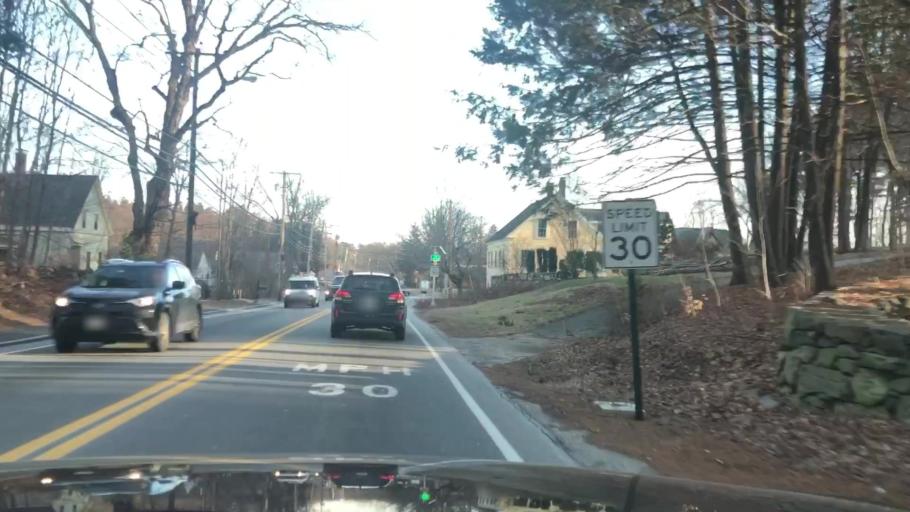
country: US
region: Massachusetts
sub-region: Worcester County
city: Bolton
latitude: 42.4355
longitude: -71.6127
